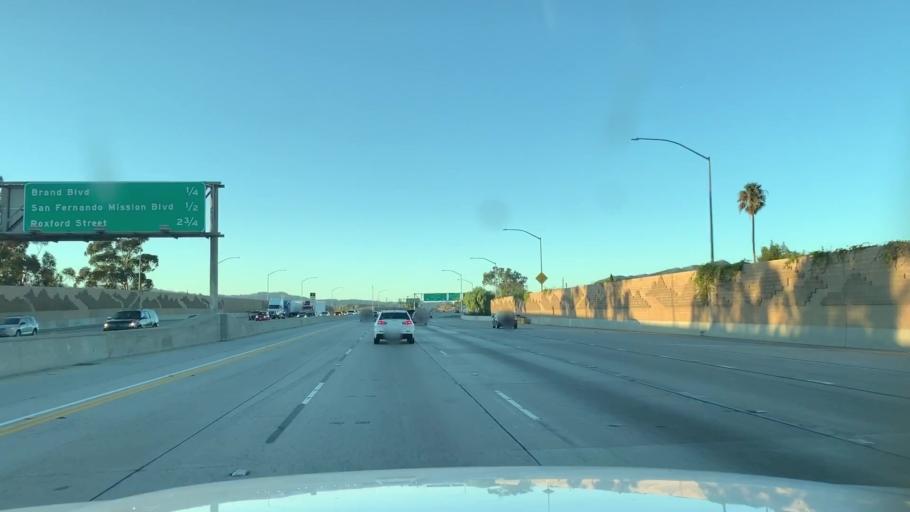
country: US
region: California
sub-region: Los Angeles County
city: San Fernando
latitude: 34.2694
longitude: -118.4462
